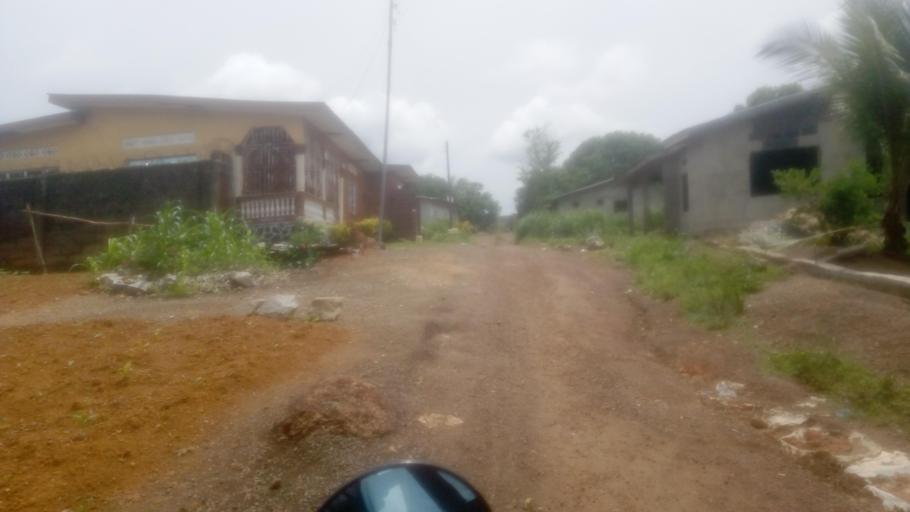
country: SL
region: Southern Province
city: Bo
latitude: 7.9548
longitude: -11.7110
